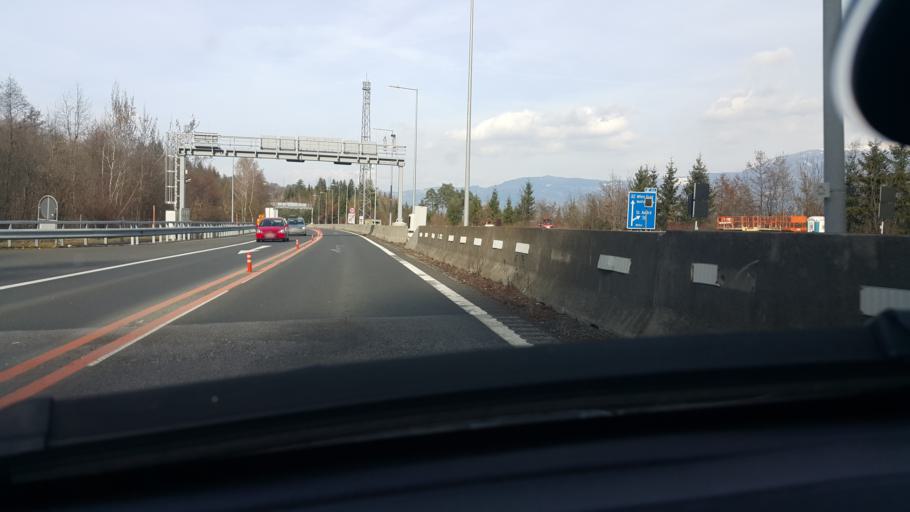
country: AT
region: Carinthia
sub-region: Politischer Bezirk Wolfsberg
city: Sankt Andrae
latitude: 46.7338
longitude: 14.8023
